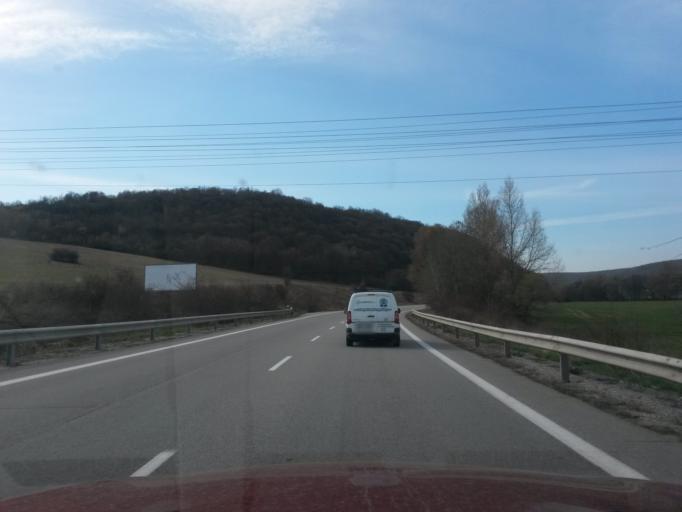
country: SK
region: Kosicky
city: Roznava
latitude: 48.5326
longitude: 20.3955
